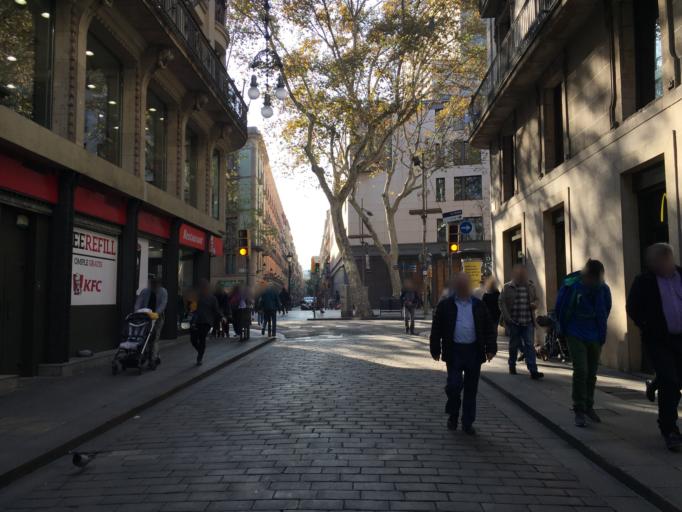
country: ES
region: Catalonia
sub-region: Provincia de Barcelona
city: Ciutat Vella
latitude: 41.3805
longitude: 2.1745
